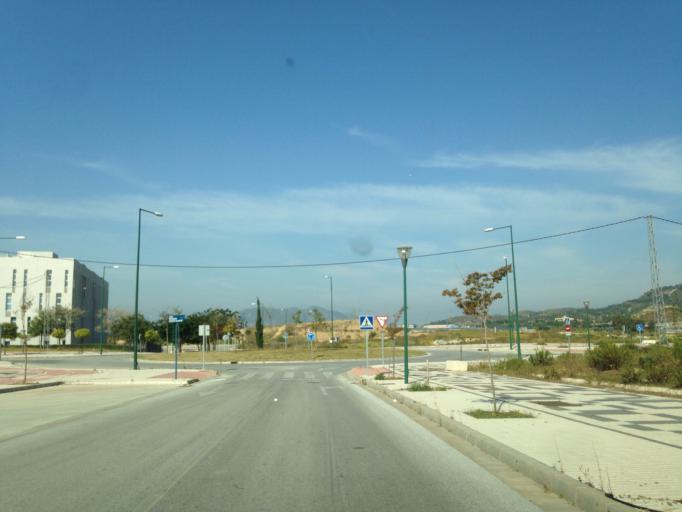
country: ES
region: Andalusia
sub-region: Provincia de Malaga
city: Malaga
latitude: 36.7174
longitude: -4.4983
